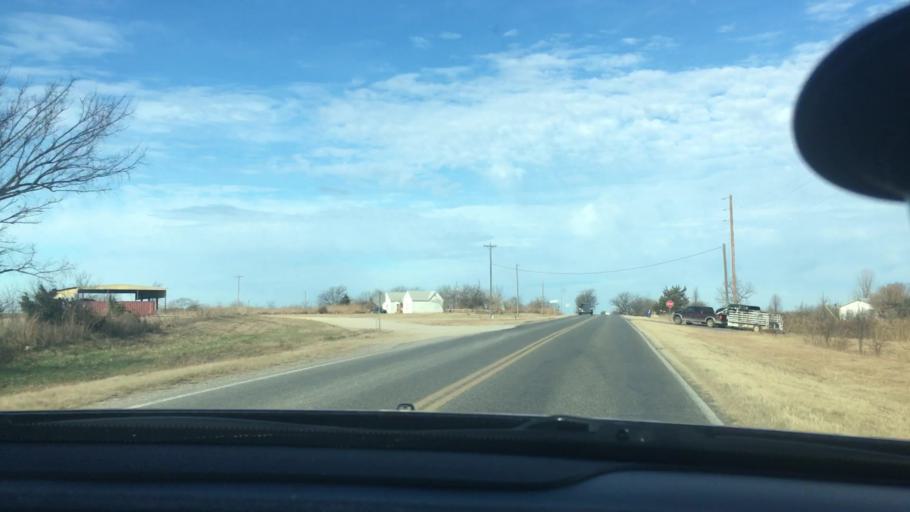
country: US
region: Oklahoma
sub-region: Seminole County
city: Konawa
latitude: 34.9705
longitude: -96.7772
